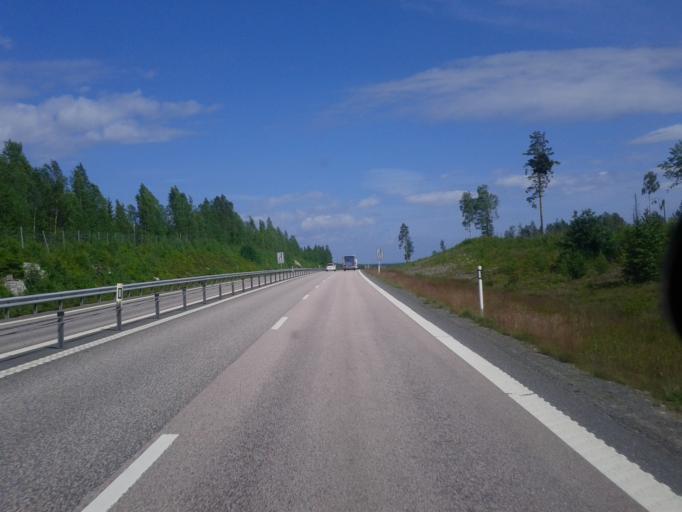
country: SE
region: Vaesternorrland
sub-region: OErnskoeldsviks Kommun
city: Husum
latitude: 63.4486
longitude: 19.2242
